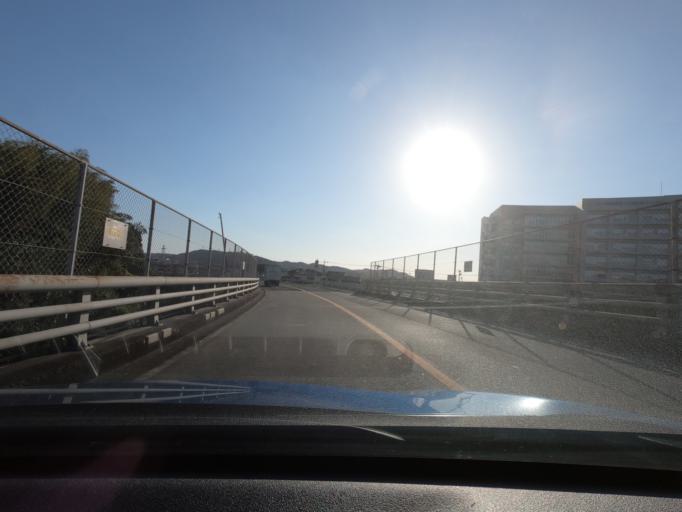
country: JP
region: Kagoshima
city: Akune
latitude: 32.0279
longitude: 130.1960
